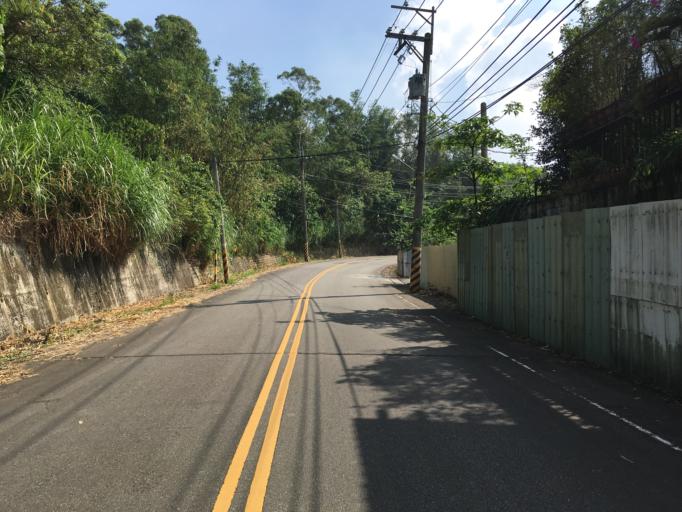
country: TW
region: Taiwan
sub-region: Taichung City
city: Taichung
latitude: 24.1763
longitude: 120.7559
